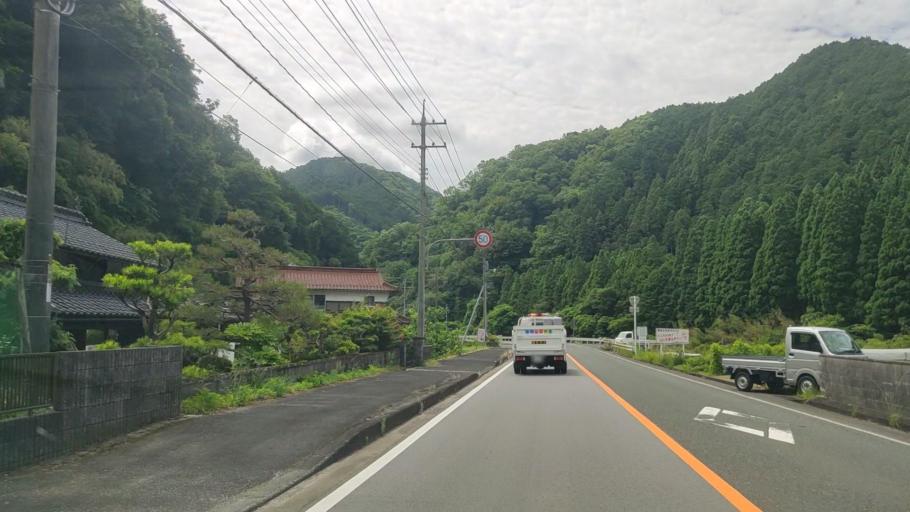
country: JP
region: Okayama
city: Niimi
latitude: 35.0717
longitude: 133.6759
